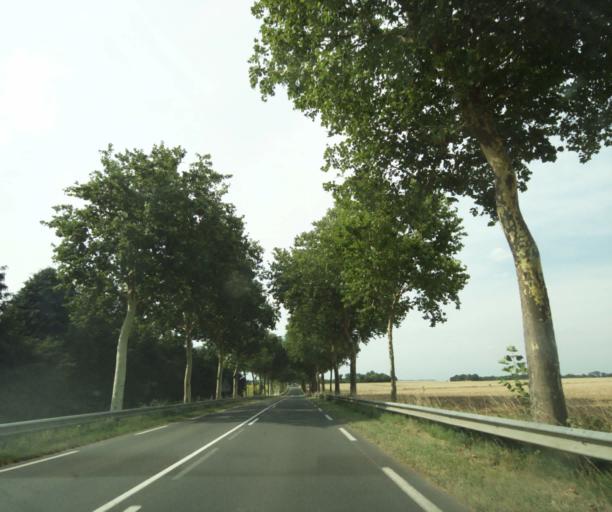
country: FR
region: Centre
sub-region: Departement d'Indre-et-Loire
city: Neuille-Pont-Pierre
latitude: 47.5663
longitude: 0.5486
